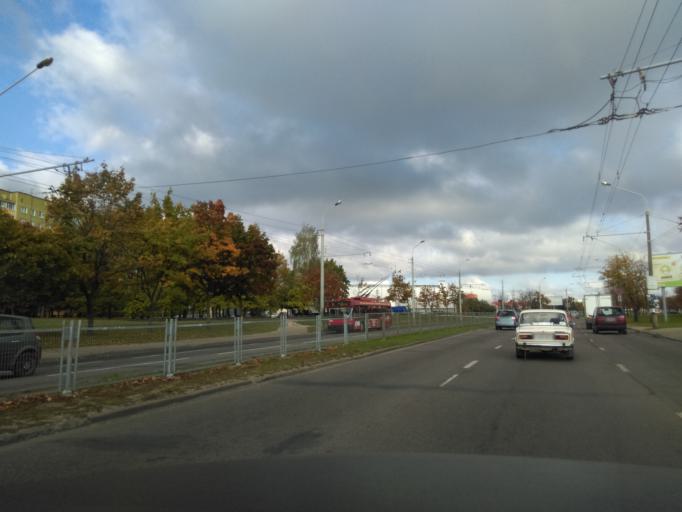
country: BY
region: Minsk
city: Minsk
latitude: 53.8728
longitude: 27.5977
